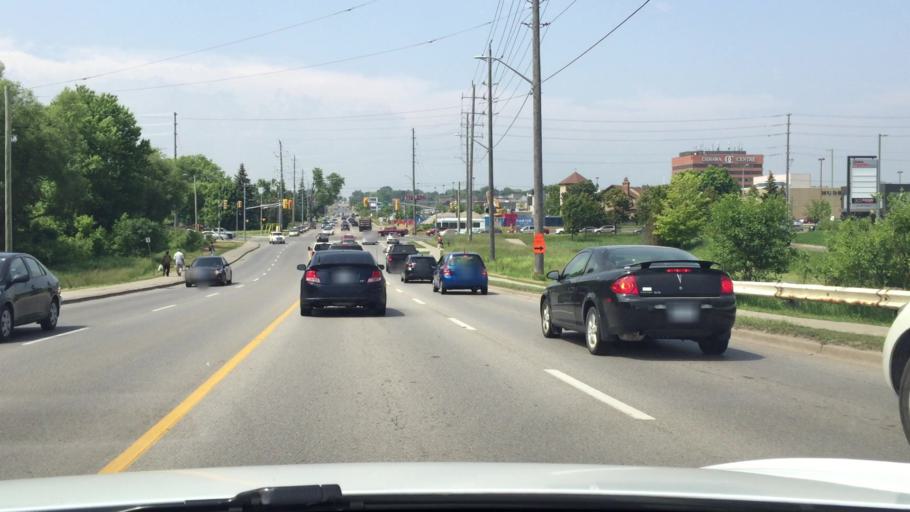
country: CA
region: Ontario
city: Oshawa
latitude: 43.8848
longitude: -78.8795
